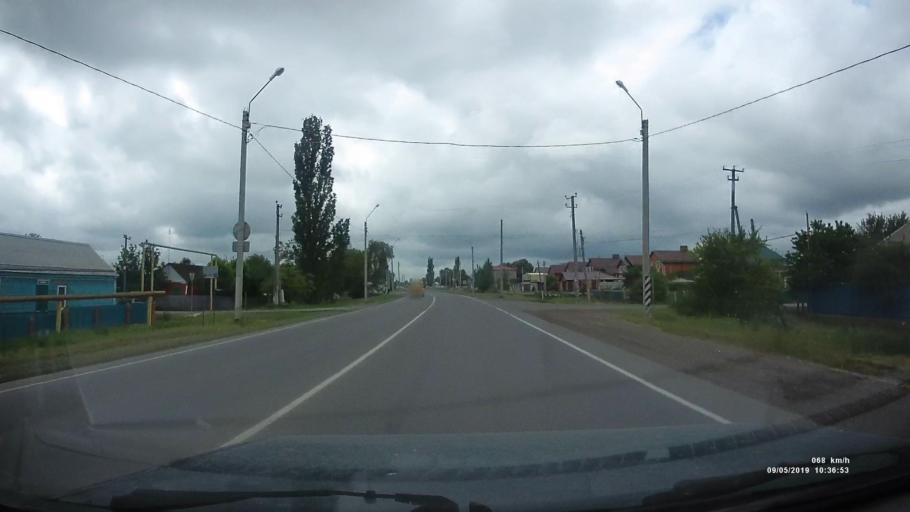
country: RU
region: Rostov
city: Peshkovo
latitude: 47.0251
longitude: 39.4055
